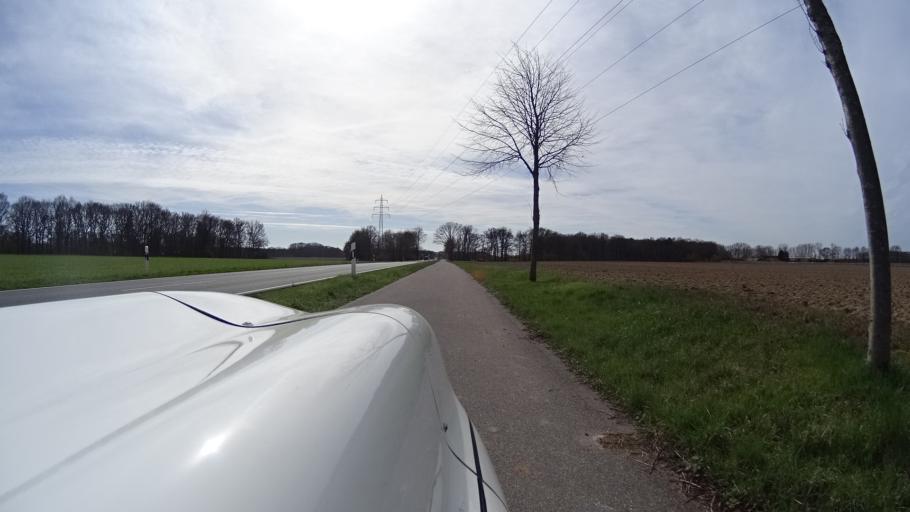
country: DE
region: North Rhine-Westphalia
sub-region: Regierungsbezirk Dusseldorf
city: Kevelaer
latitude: 51.6110
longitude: 6.2538
